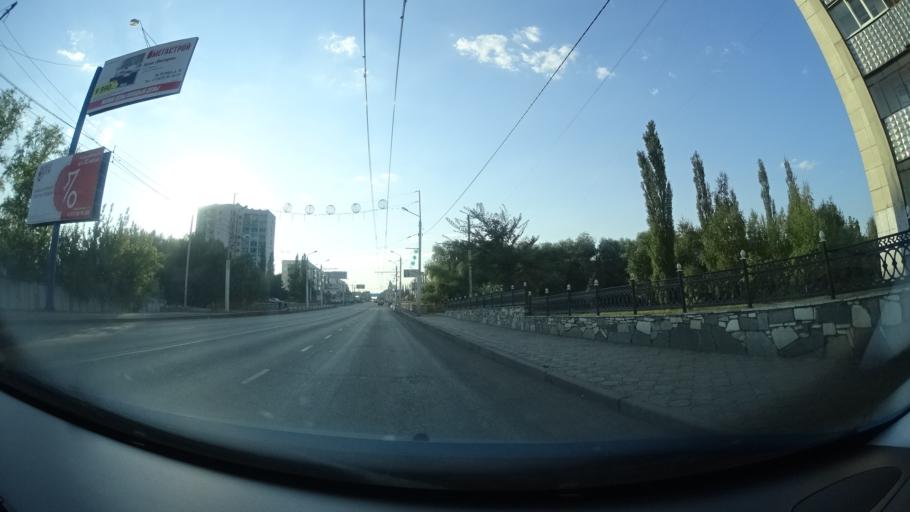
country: RU
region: Bashkortostan
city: Sterlitamak
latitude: 53.6219
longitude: 55.9553
